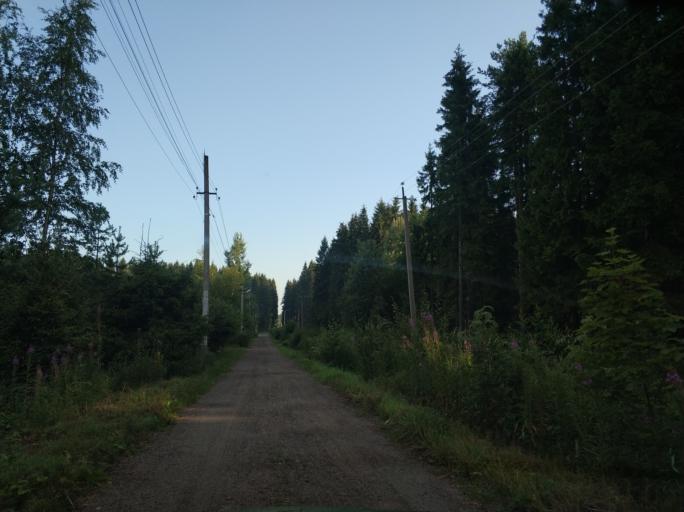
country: RU
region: Leningrad
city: Shcheglovo
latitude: 60.0542
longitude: 30.7508
